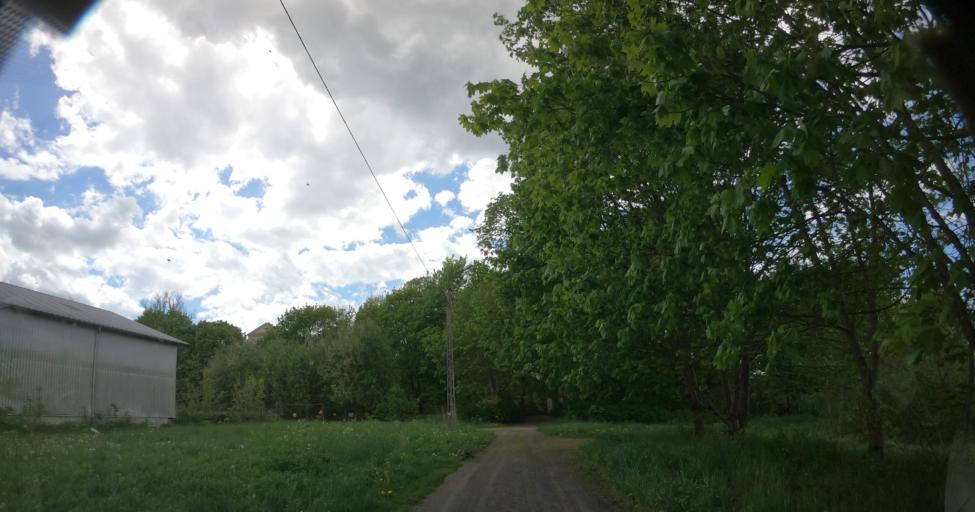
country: PL
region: West Pomeranian Voivodeship
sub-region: Powiat drawski
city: Drawsko Pomorskie
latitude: 53.5856
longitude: 15.7304
